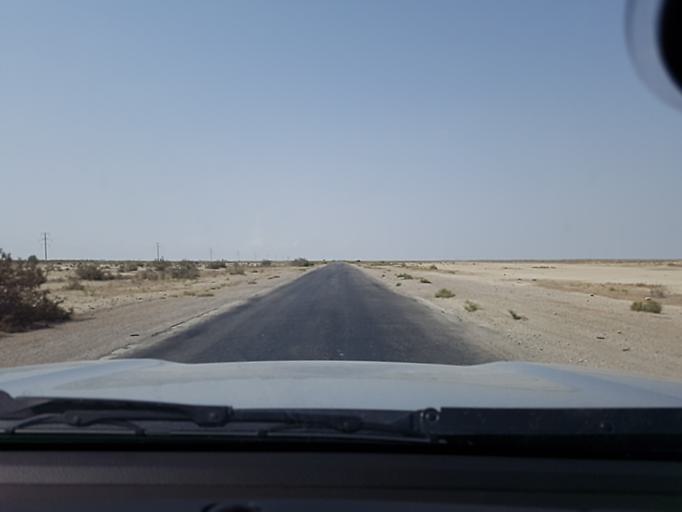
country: TM
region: Balkan
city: Gumdag
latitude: 38.7809
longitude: 54.5929
